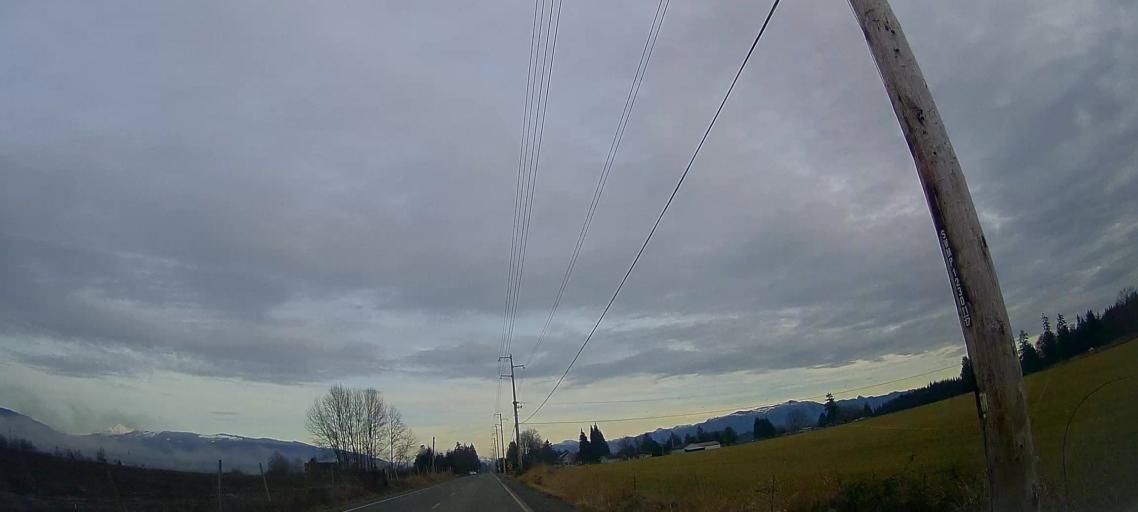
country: US
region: Washington
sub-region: Skagit County
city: Burlington
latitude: 48.5168
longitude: -122.4370
